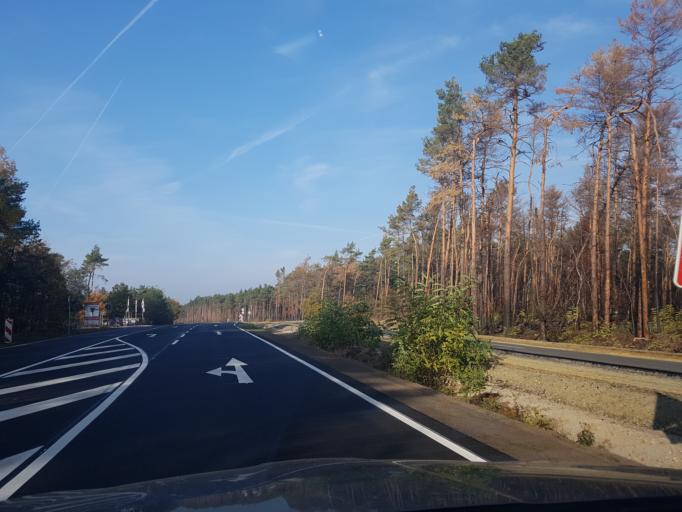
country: DE
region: Brandenburg
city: Elsterwerda
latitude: 51.4859
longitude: 13.4881
